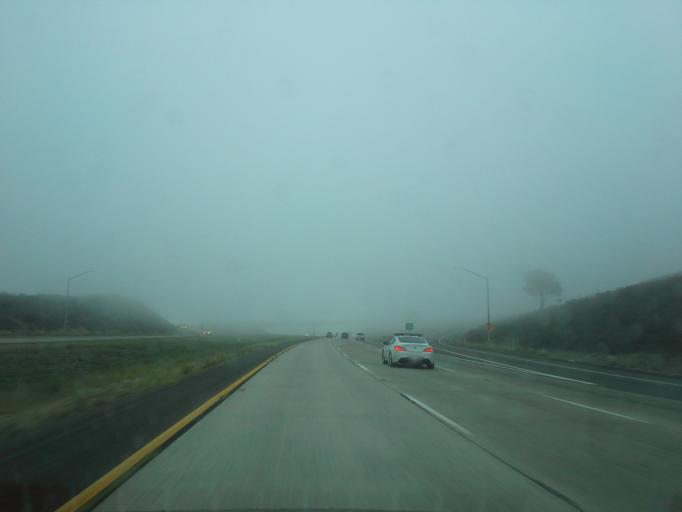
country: US
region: California
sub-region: San Diego County
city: Descanso
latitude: 32.8383
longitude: -116.6861
